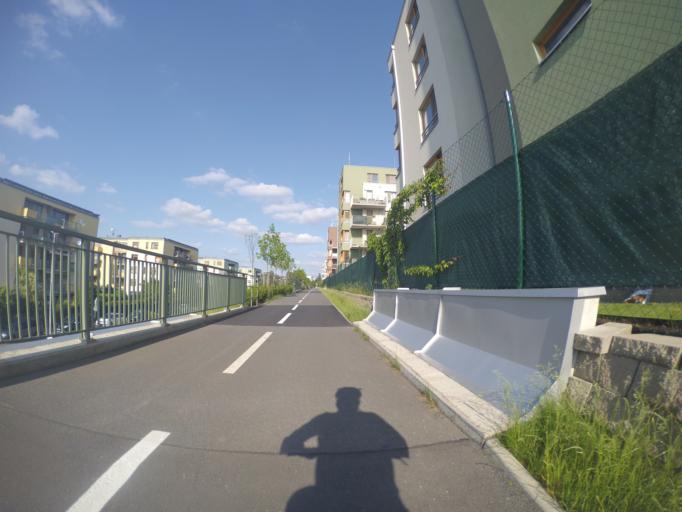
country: CZ
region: Praha
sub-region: Praha 9
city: Vysocany
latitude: 50.1057
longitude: 14.5216
